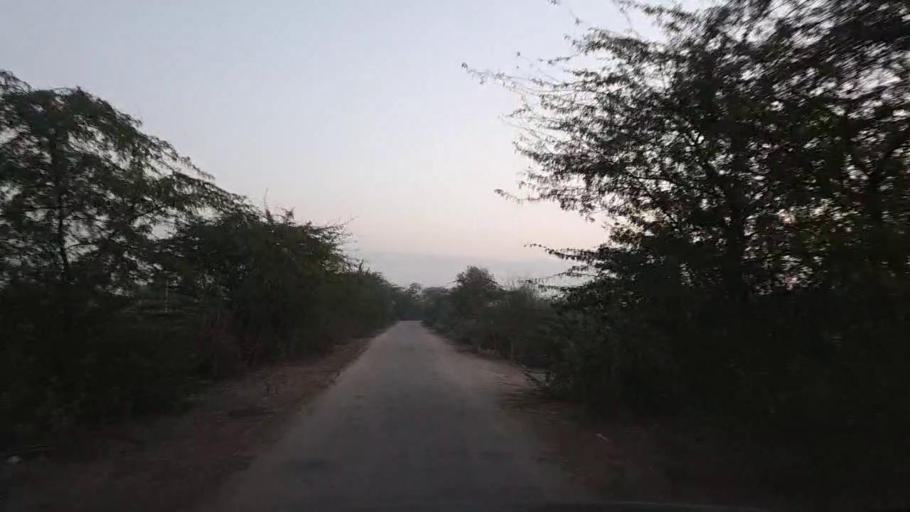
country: PK
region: Sindh
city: Daur
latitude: 26.4846
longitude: 68.4906
